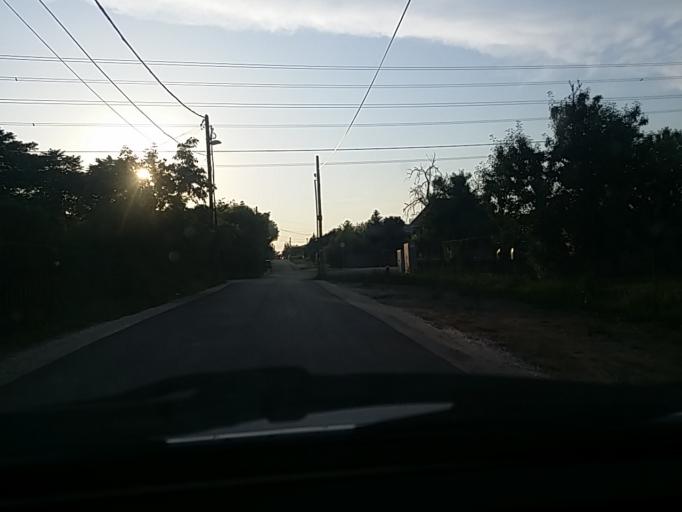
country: HU
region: Pest
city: Urom
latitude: 47.5823
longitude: 19.0158
